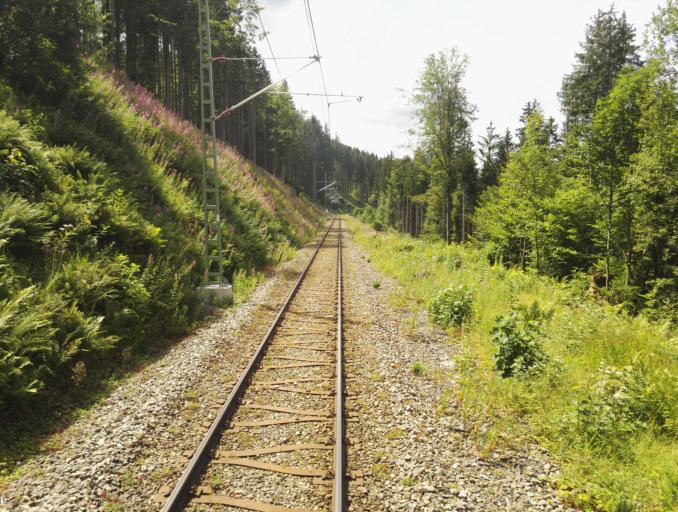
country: DE
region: Baden-Wuerttemberg
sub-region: Freiburg Region
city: Hinterzarten
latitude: 47.8873
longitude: 8.1437
